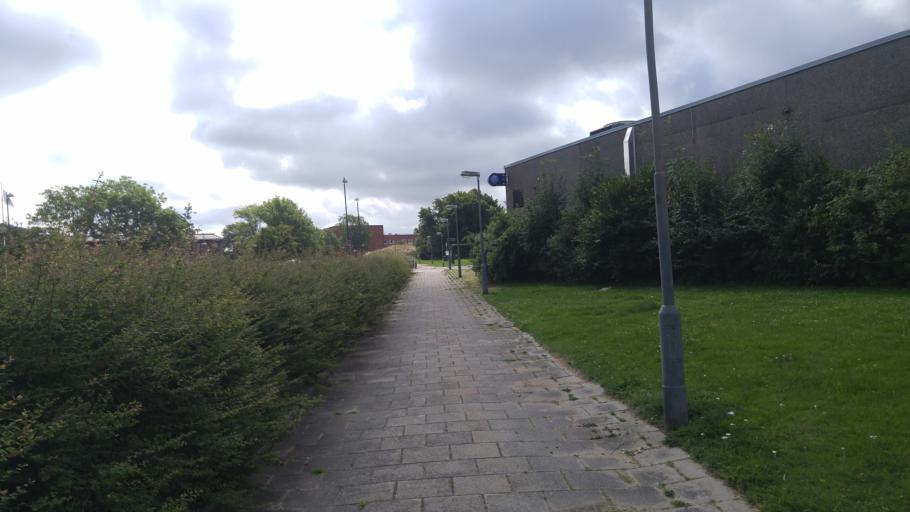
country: SE
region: Skane
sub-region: Burlovs Kommun
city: Arloev
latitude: 55.5823
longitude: 13.0651
